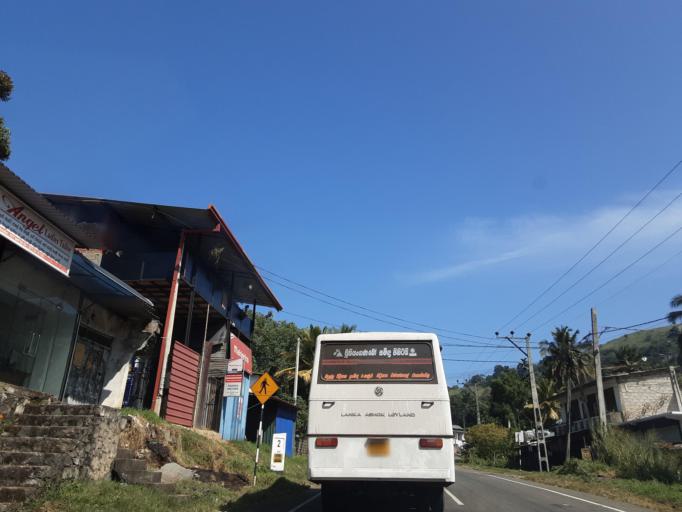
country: LK
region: Uva
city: Badulla
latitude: 7.0055
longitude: 81.0564
